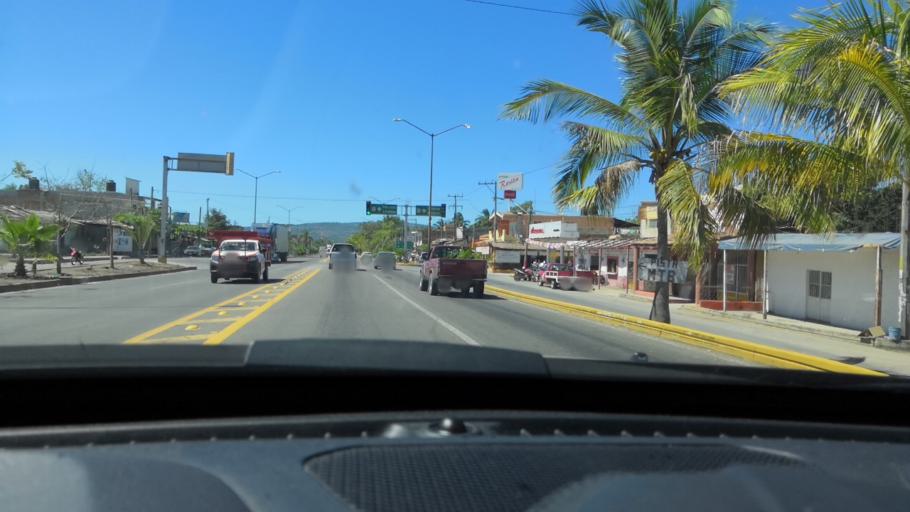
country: MX
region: Nayarit
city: Las Varas
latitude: 21.1834
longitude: -105.1300
